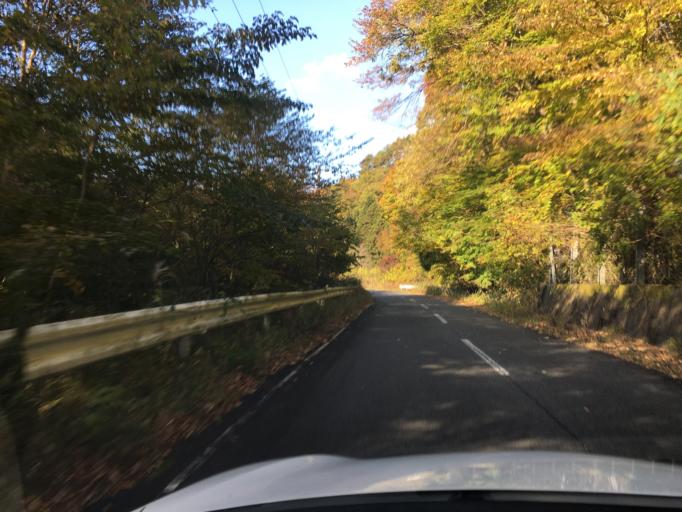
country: JP
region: Fukushima
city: Iwaki
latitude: 37.2420
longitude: 140.7625
